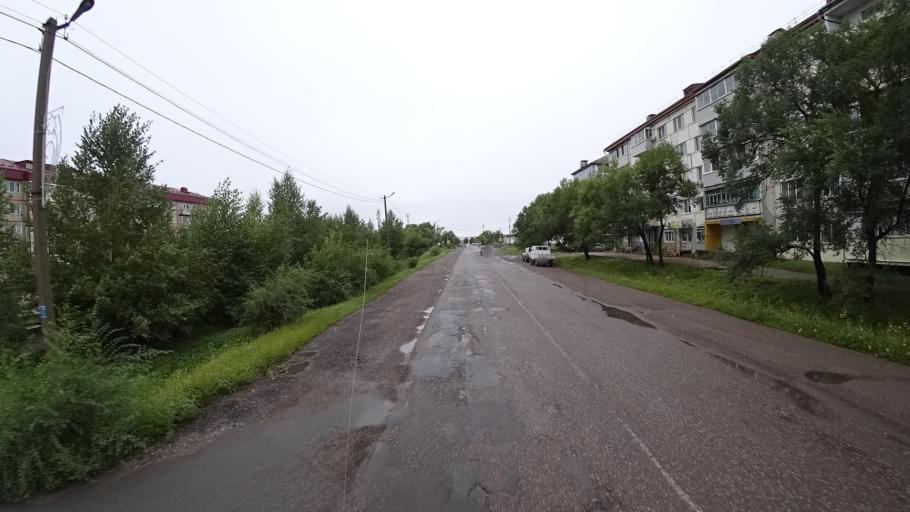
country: RU
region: Primorskiy
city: Monastyrishche
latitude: 44.2041
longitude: 132.4468
